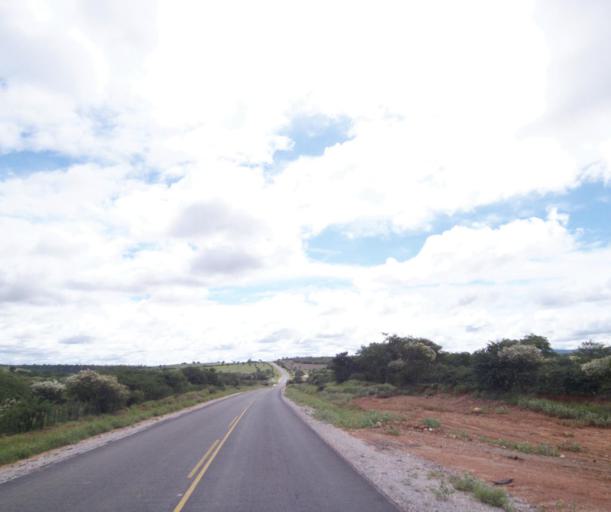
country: BR
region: Bahia
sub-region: Brumado
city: Brumado
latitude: -14.1506
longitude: -41.4989
